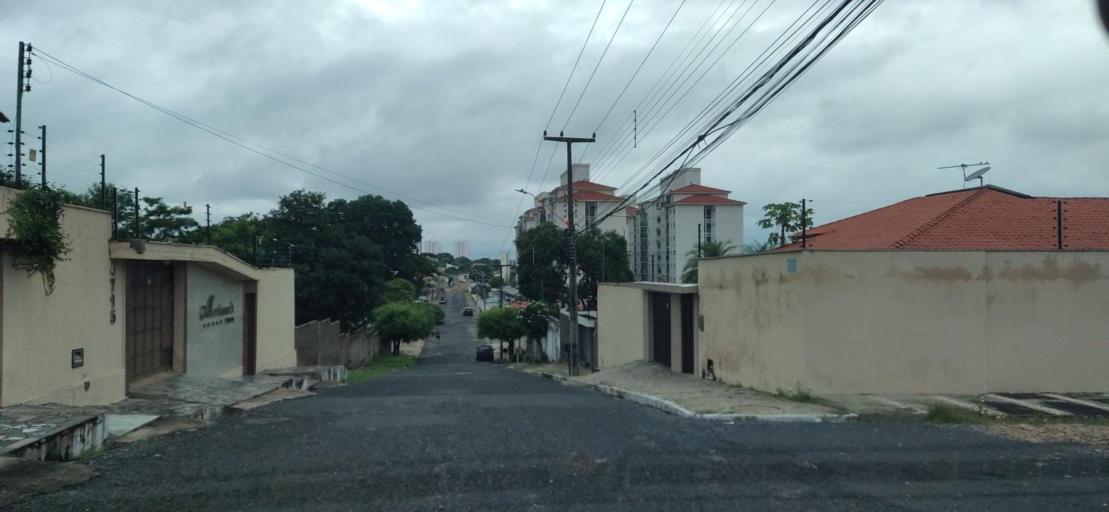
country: BR
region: Piaui
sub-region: Teresina
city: Teresina
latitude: -5.0720
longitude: -42.7590
